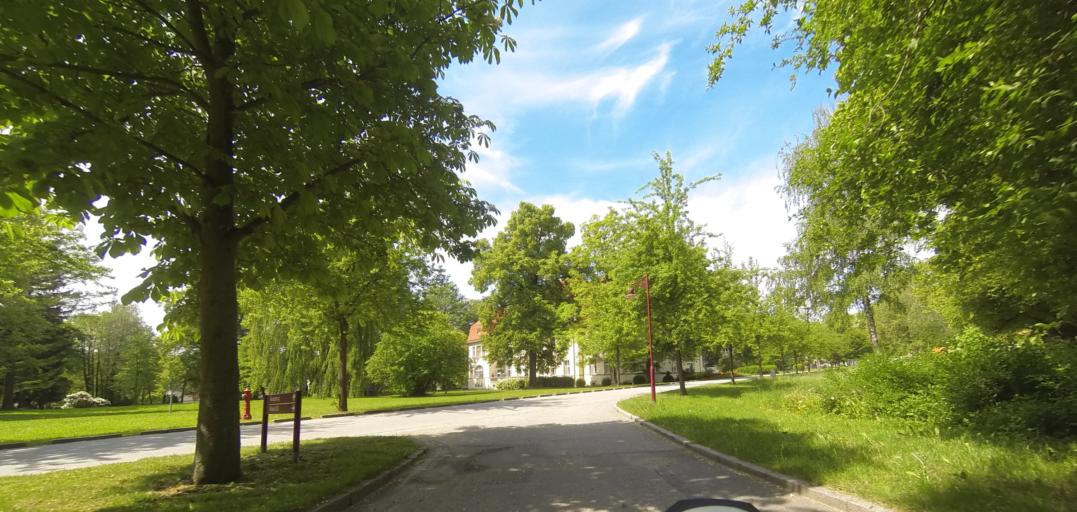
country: DE
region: Saxony
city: Arnsdorf
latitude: 51.0932
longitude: 13.9998
